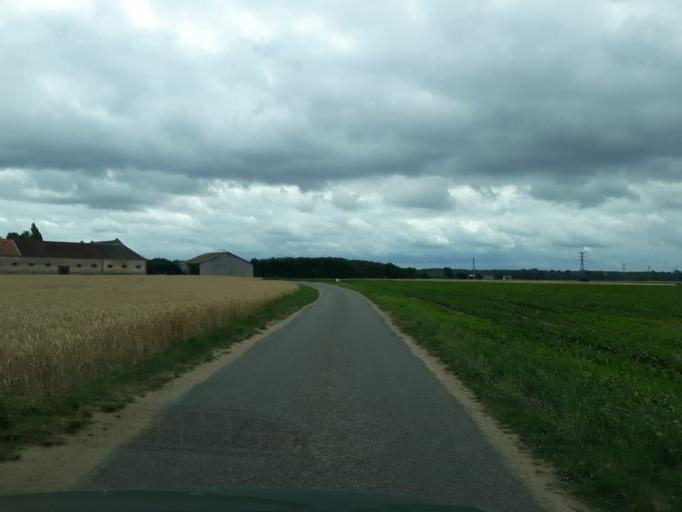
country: FR
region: Centre
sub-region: Departement du Loiret
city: Saint-Cyr-en-Val
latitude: 47.8470
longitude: 1.9851
